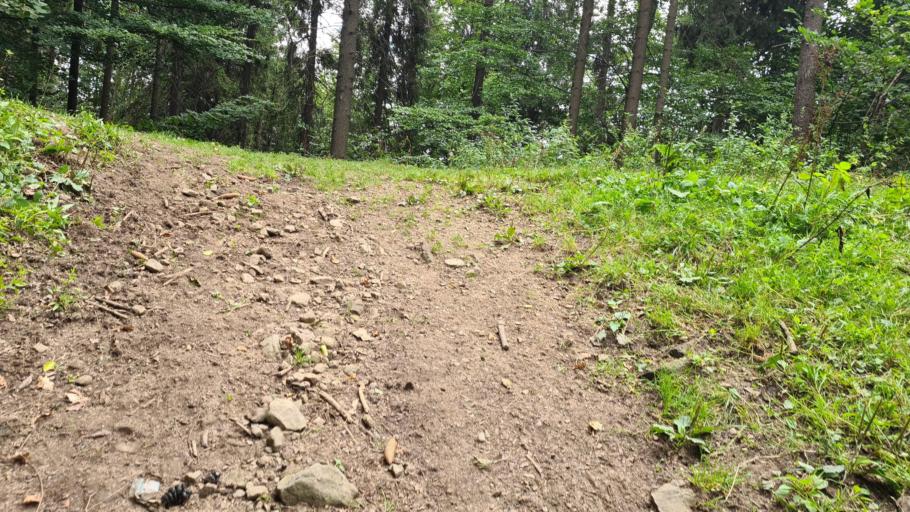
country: PL
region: Lesser Poland Voivodeship
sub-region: Powiat nowosadecki
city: Piwniczna-Zdroj
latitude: 49.4354
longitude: 20.7235
